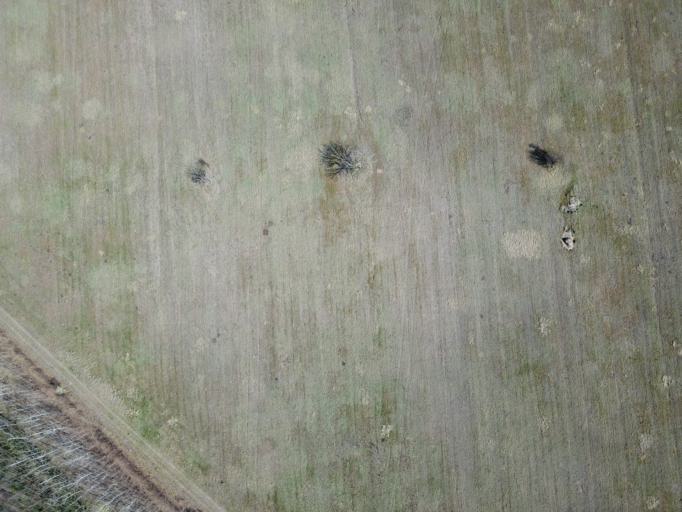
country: HU
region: Pest
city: Budakalasz
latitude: 47.6106
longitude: 19.0665
